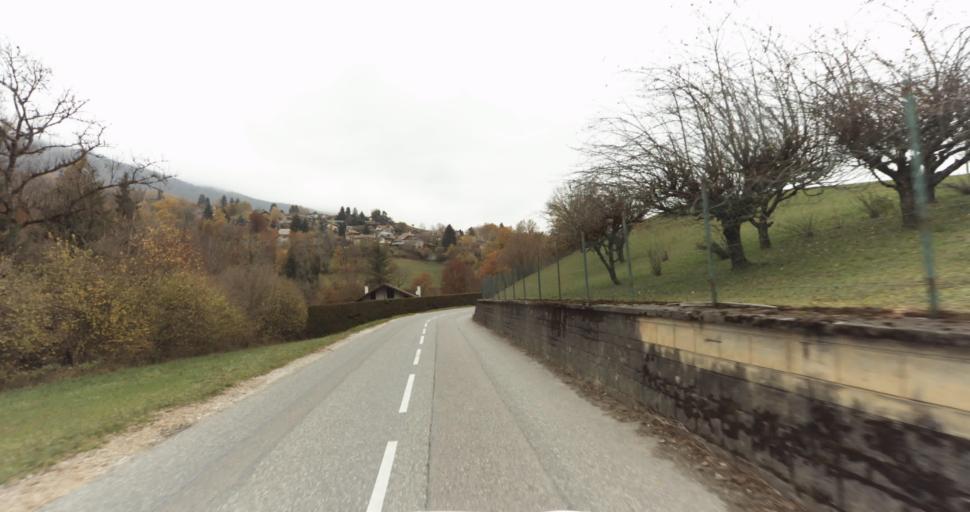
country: FR
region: Rhone-Alpes
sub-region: Departement de la Haute-Savoie
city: Saint-Jorioz
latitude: 45.8218
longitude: 6.1481
